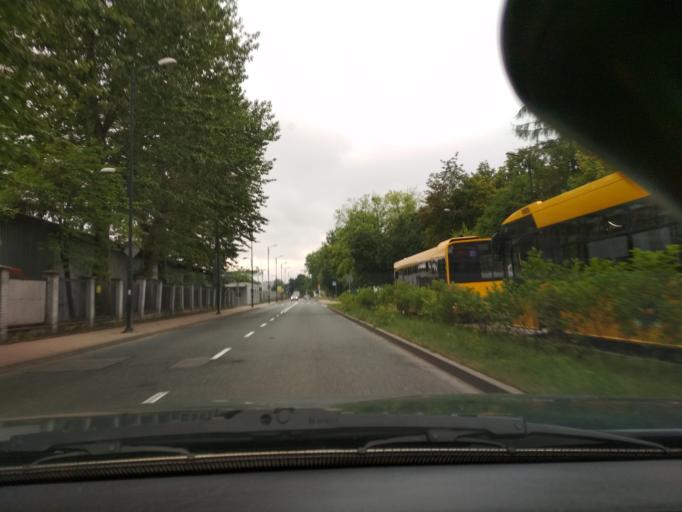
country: PL
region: Silesian Voivodeship
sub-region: Gliwice
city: Gliwice
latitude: 50.2748
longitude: 18.6731
